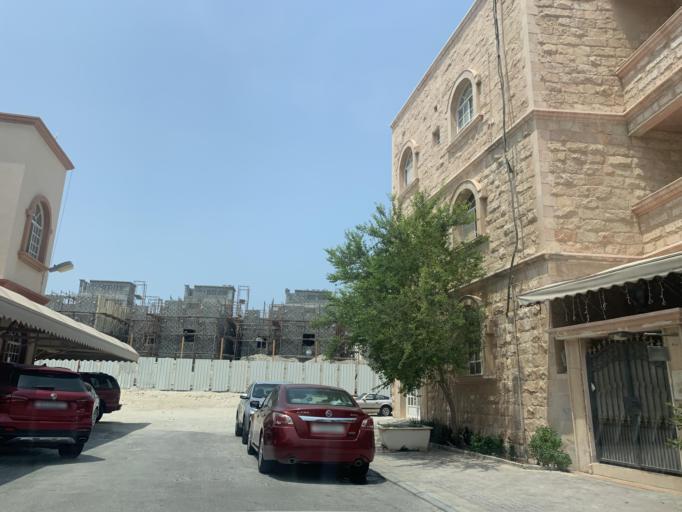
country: BH
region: Muharraq
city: Al Hadd
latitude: 26.2775
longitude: 50.6502
